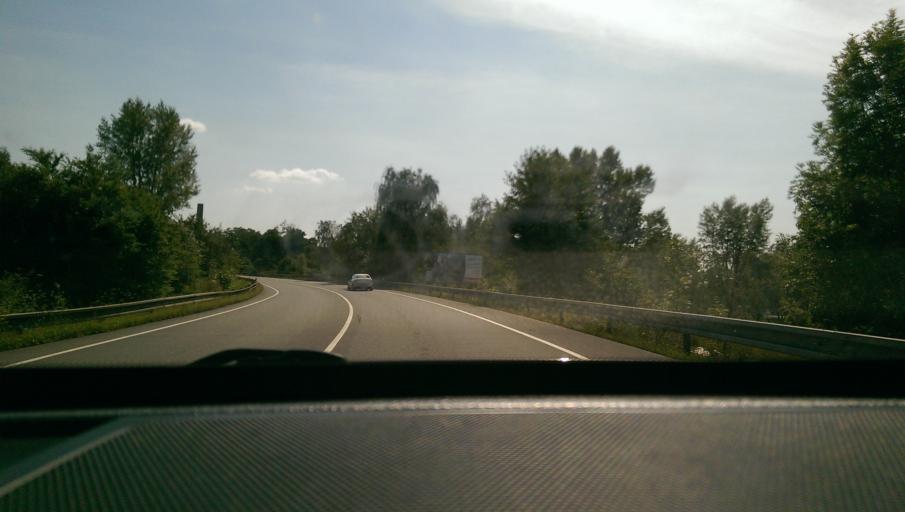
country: CZ
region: Moravskoslezsky
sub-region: Okres Ostrava-Mesto
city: Ostrava
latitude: 49.8471
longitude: 18.2422
